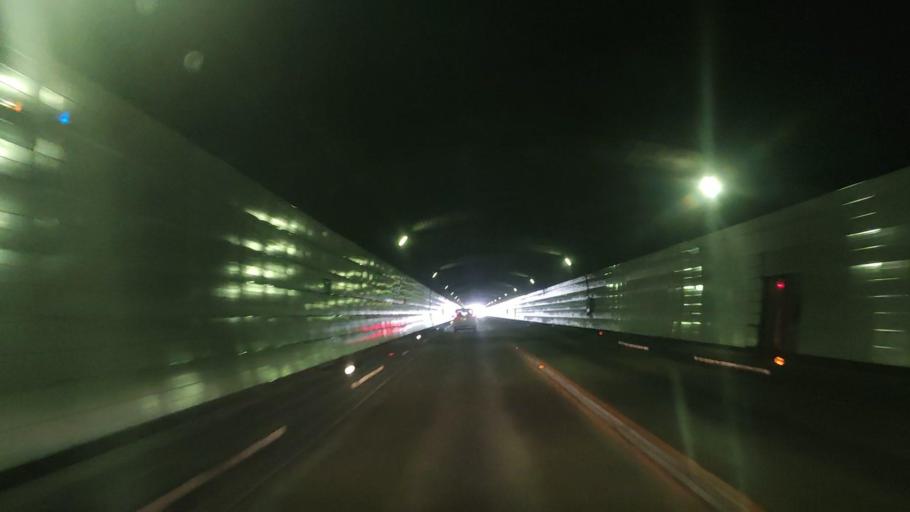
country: JP
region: Kumamoto
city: Hitoyoshi
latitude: 32.0922
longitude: 130.8022
